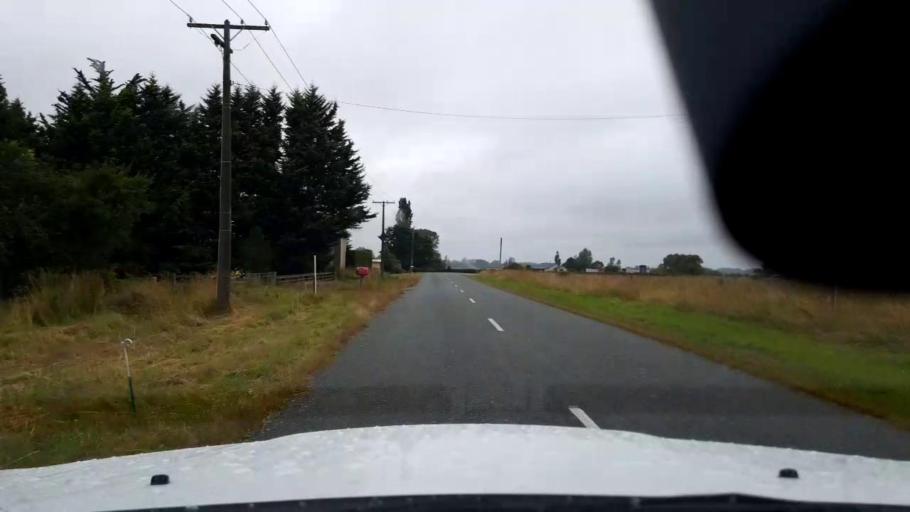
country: NZ
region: Canterbury
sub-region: Timaru District
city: Pleasant Point
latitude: -44.2511
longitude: 171.2333
